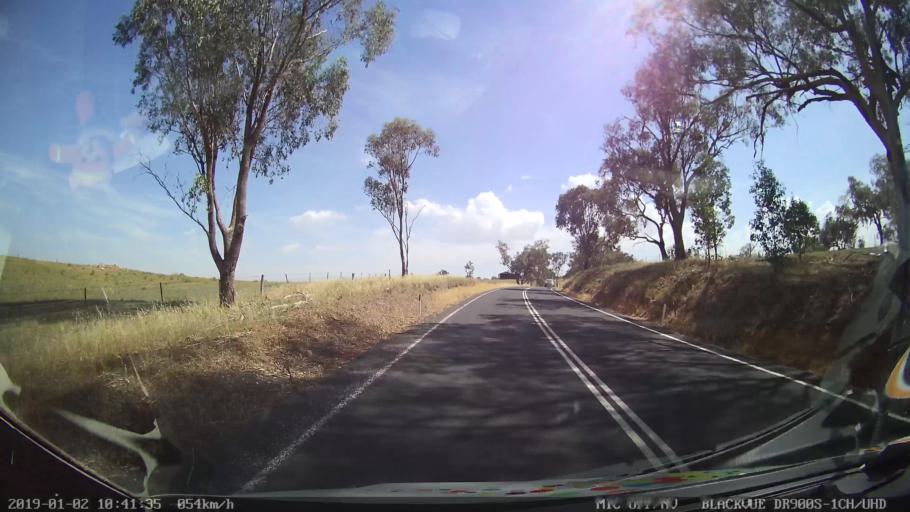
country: AU
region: New South Wales
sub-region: Cootamundra
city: Cootamundra
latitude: -34.7928
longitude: 148.3066
